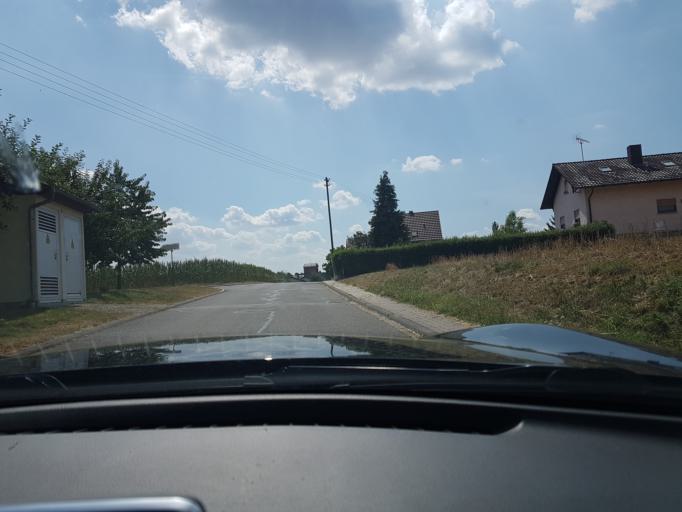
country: DE
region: Baden-Wuerttemberg
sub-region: Karlsruhe Region
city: Fahrenbach
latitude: 49.4124
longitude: 9.1729
